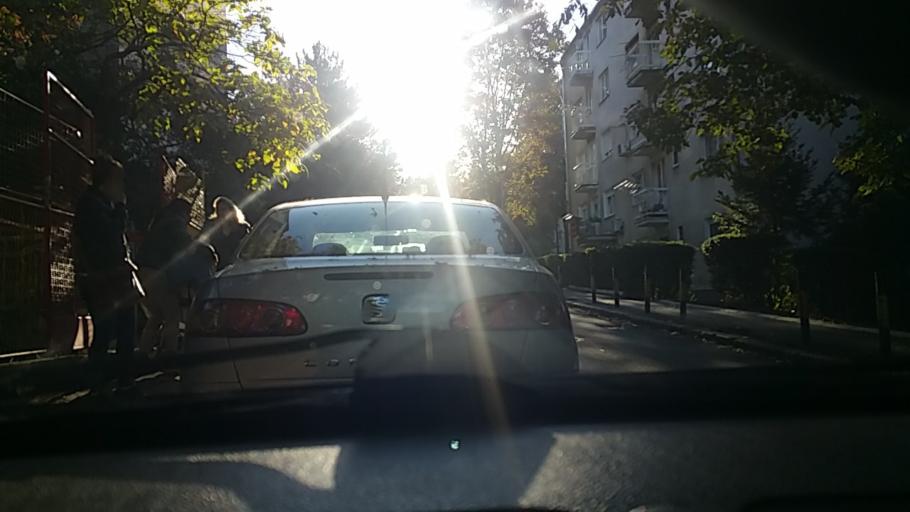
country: RS
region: Central Serbia
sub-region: Belgrade
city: Rakovica
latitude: 44.7508
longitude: 20.4574
